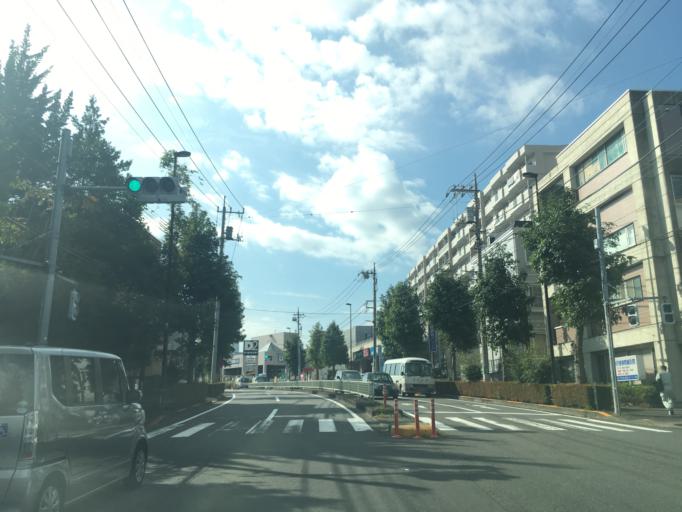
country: JP
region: Tokyo
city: Hino
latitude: 35.6164
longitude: 139.4124
